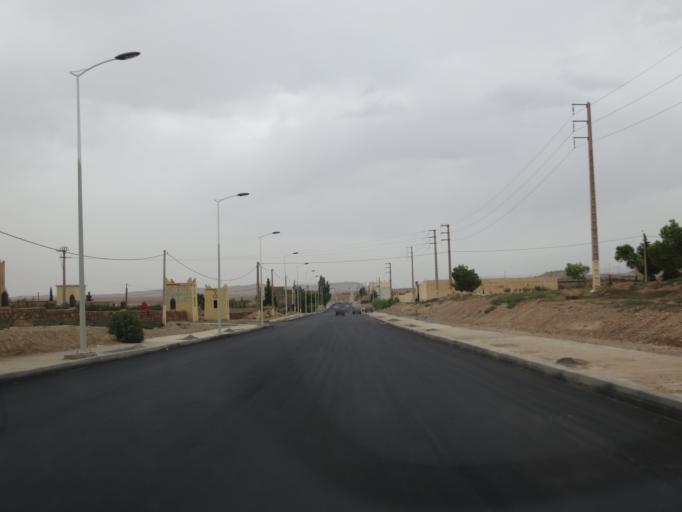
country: MA
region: Meknes-Tafilalet
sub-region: Khenifra
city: Midelt
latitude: 32.7062
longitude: -4.7888
